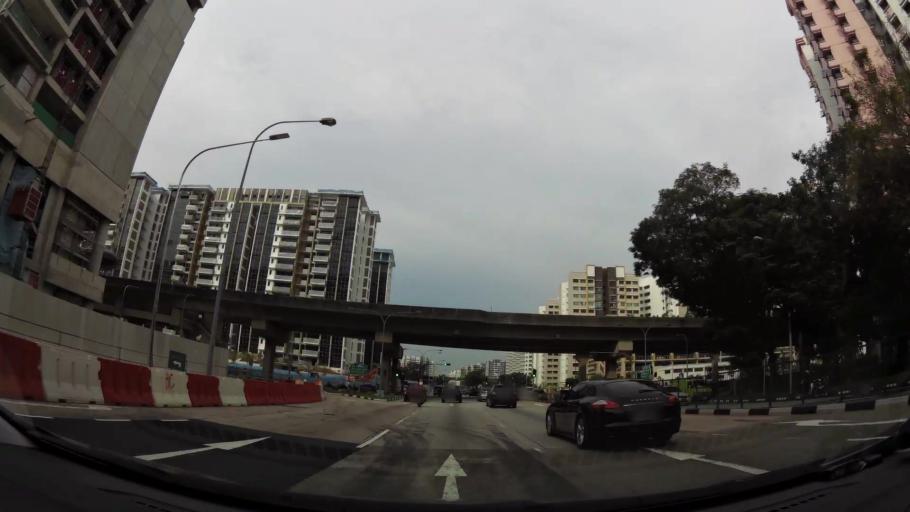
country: MY
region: Johor
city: Kampung Pasir Gudang Baru
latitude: 1.3956
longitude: 103.8944
